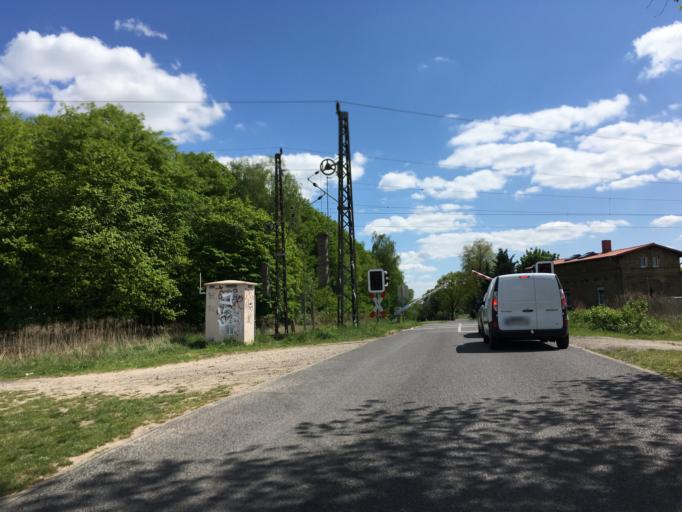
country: DE
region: Brandenburg
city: Biesenthal
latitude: 52.7393
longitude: 13.6577
